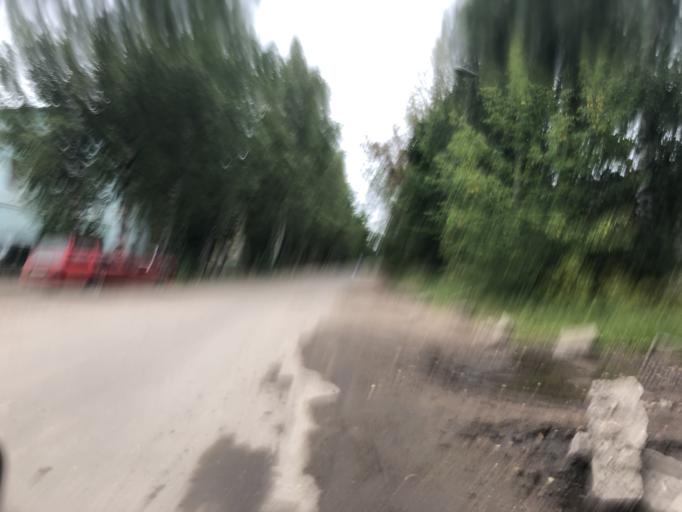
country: RU
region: Tverskaya
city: Rzhev
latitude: 56.2415
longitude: 34.3300
